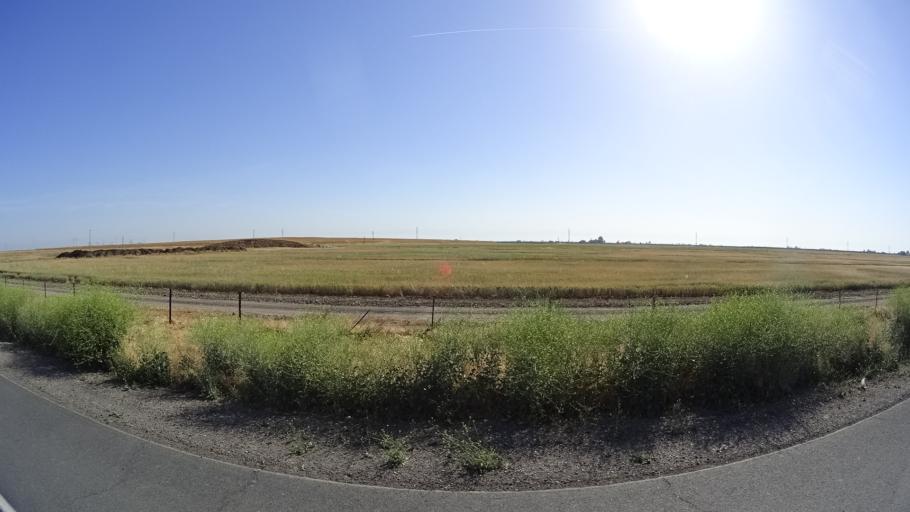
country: US
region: California
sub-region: Kings County
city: Corcoran
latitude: 36.1286
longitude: -119.5784
